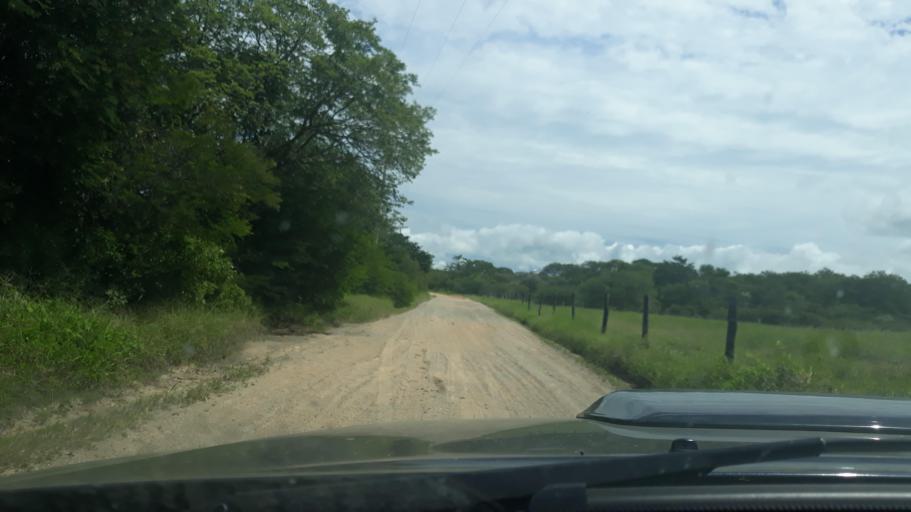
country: BR
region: Bahia
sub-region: Riacho De Santana
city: Riacho de Santana
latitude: -13.8846
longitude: -43.0214
